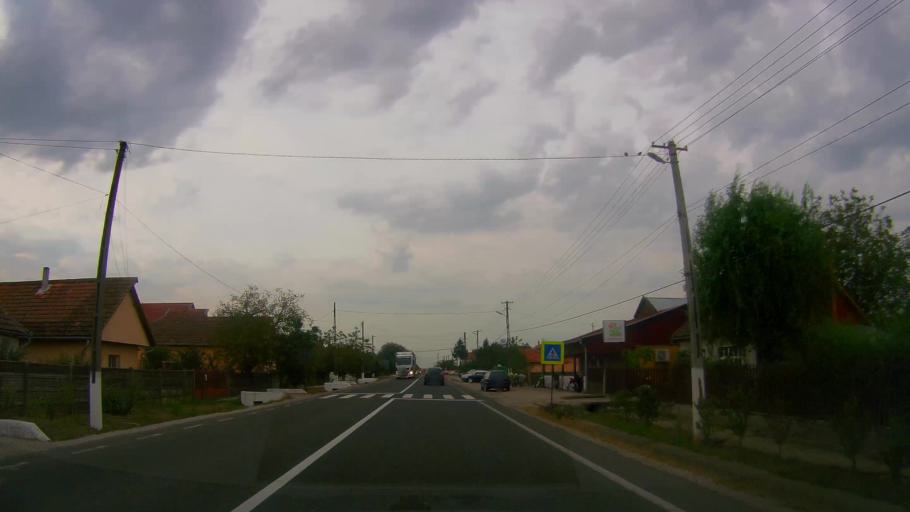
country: RO
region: Satu Mare
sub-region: Comuna Acas
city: Acas
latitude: 47.5287
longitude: 22.7824
